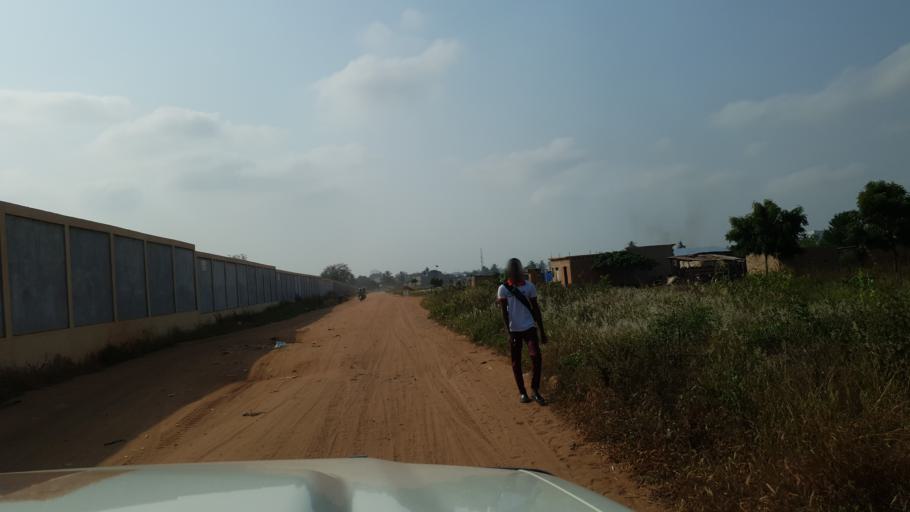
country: TG
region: Maritime
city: Lome
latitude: 6.1690
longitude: 1.2103
